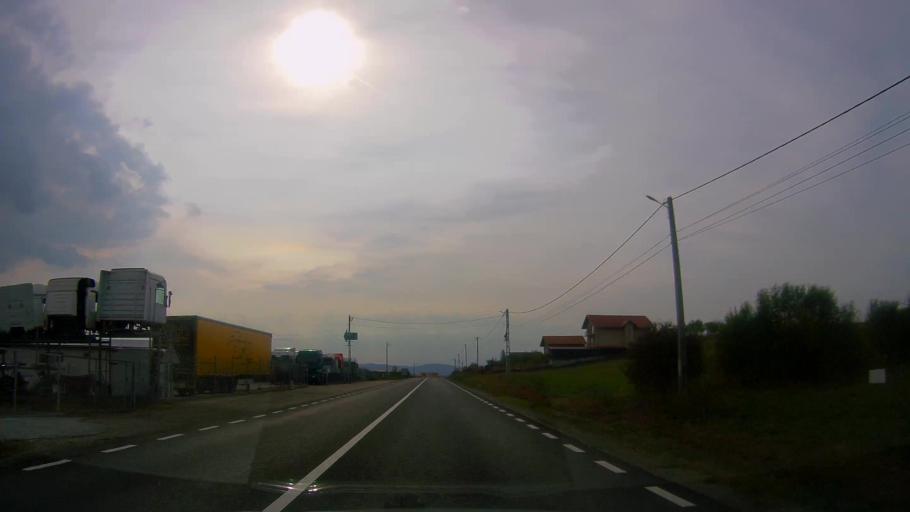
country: RO
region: Salaj
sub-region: Comuna Hereclean
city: Hereclean
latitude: 47.2536
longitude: 22.9804
